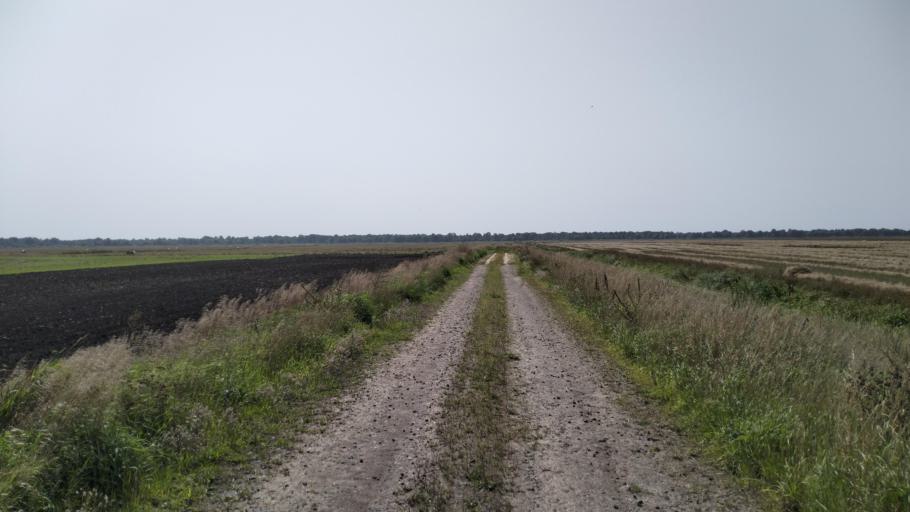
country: BY
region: Brest
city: Davyd-Haradok
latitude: 51.9790
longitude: 27.1632
